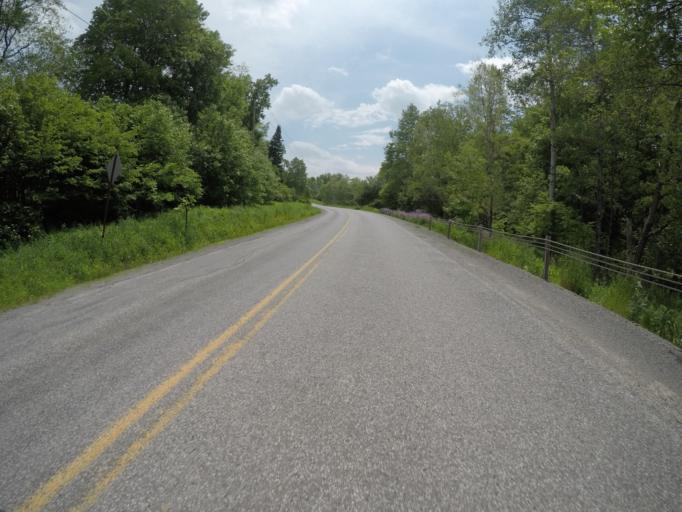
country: US
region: New York
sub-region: Delaware County
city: Stamford
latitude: 42.2004
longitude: -74.6783
